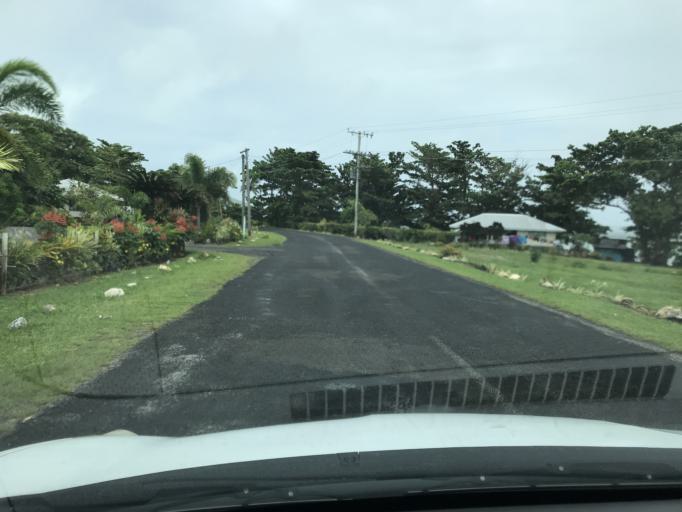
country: WS
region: Va`a-o-Fonoti
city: Samamea
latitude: -14.0455
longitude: -171.4385
